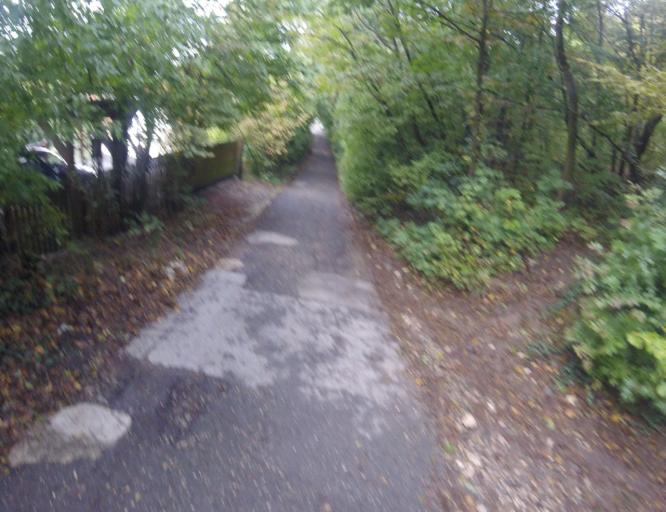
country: HU
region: Pest
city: Csobanka
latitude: 47.6436
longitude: 18.9717
